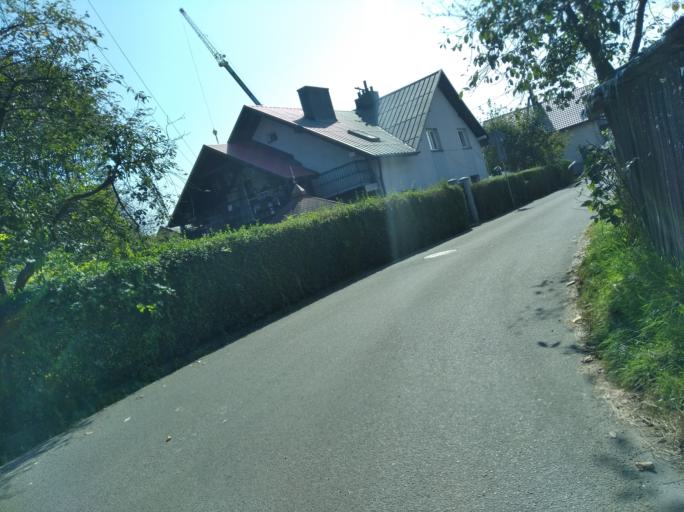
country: PL
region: Subcarpathian Voivodeship
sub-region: Powiat strzyzowski
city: Czudec
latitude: 49.9472
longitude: 21.8391
